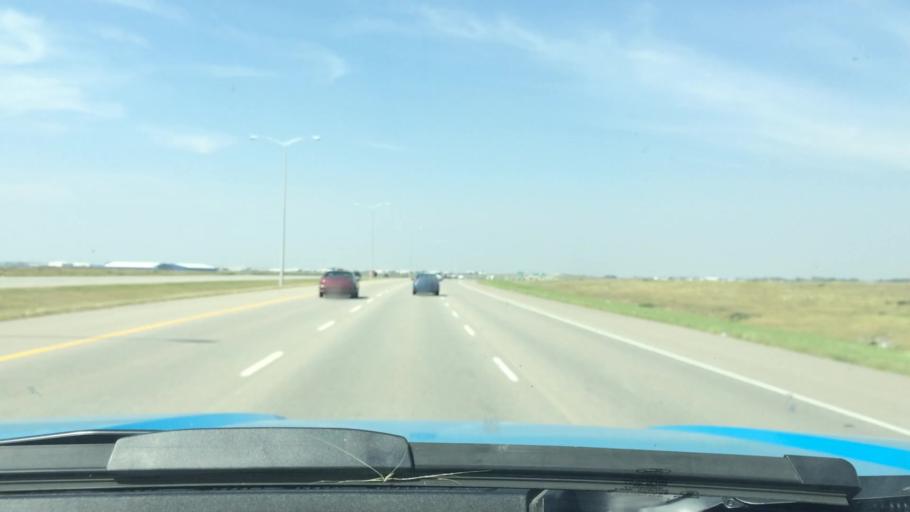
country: CA
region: Alberta
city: Chestermere
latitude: 50.9284
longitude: -113.9187
